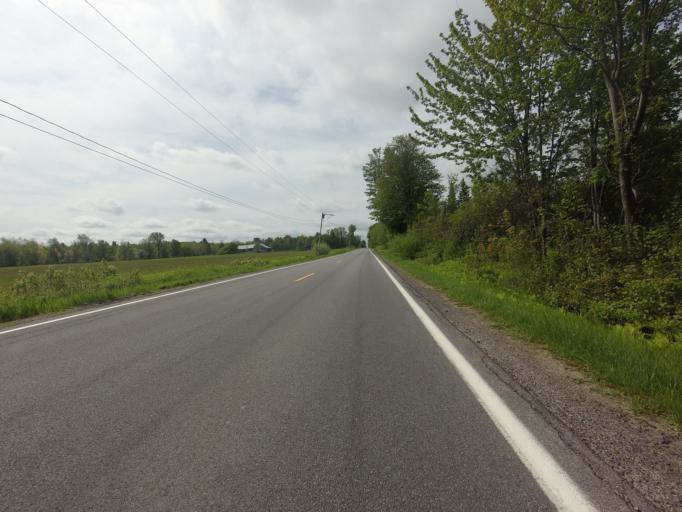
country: CA
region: Ontario
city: Cornwall
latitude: 44.7384
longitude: -74.6659
